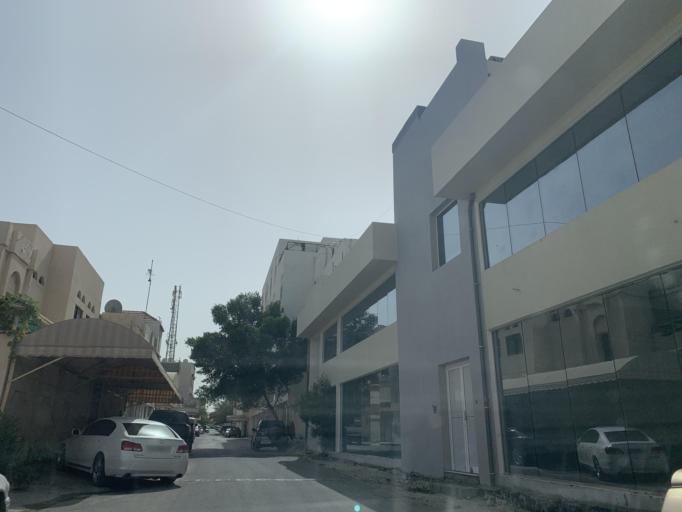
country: BH
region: Northern
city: Ar Rifa'
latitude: 26.1259
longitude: 50.5725
